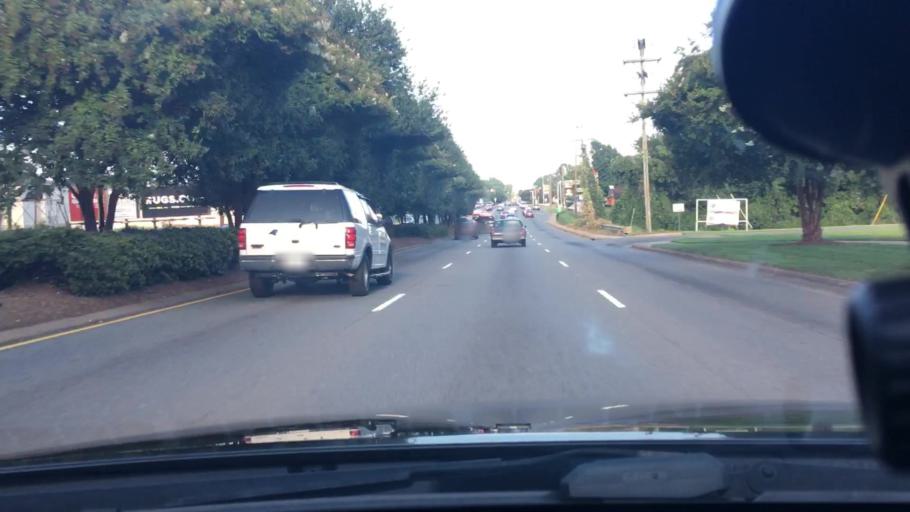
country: US
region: North Carolina
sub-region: Mecklenburg County
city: Matthews
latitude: 35.2031
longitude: -80.7421
